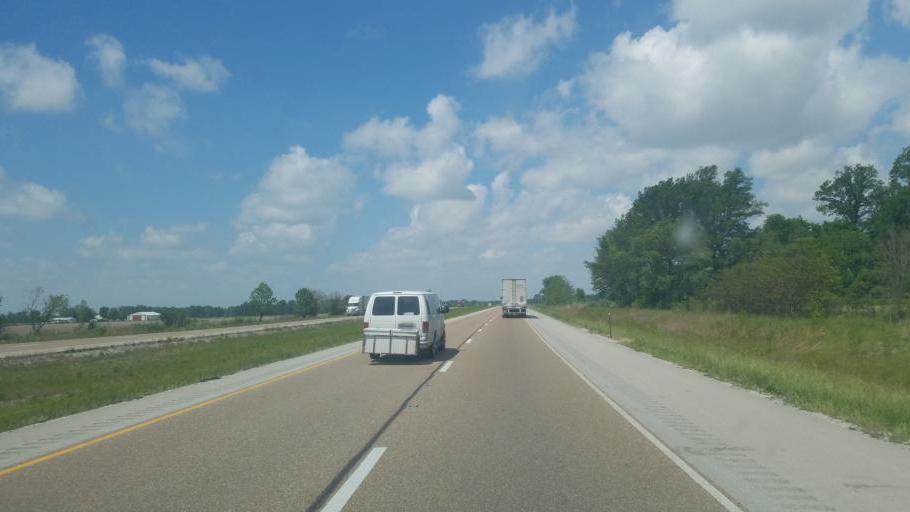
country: US
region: Illinois
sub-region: Cumberland County
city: Greenup
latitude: 39.2747
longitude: -88.0941
